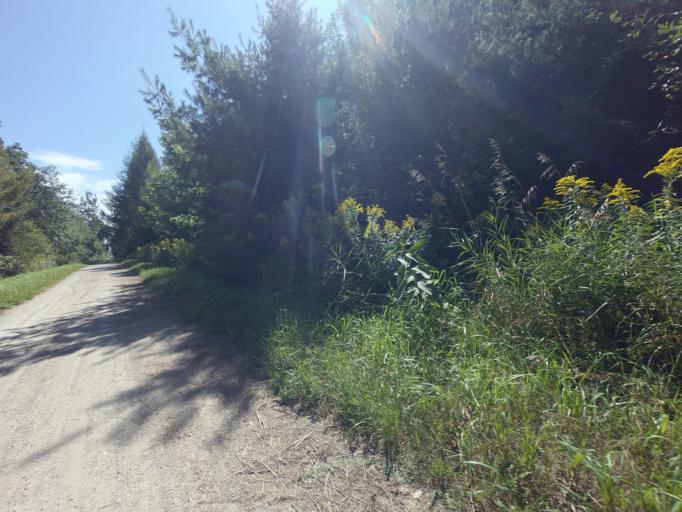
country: CA
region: Ontario
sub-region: Wellington County
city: Guelph
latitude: 43.7366
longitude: -80.3452
